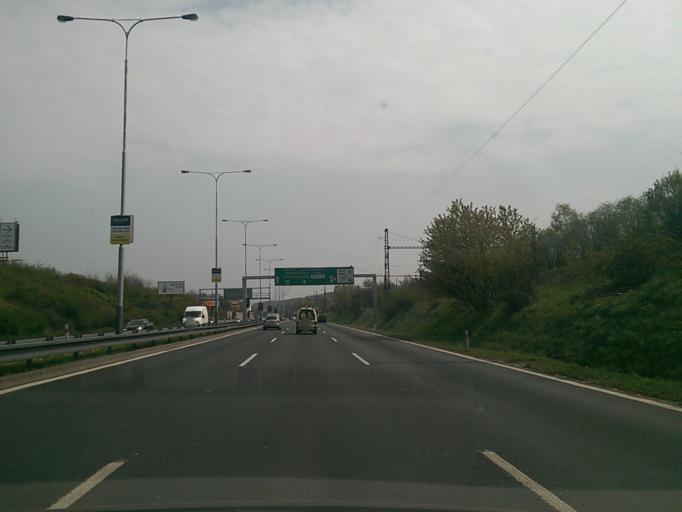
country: CZ
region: Praha
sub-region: Praha 4
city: Hodkovicky
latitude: 50.0328
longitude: 14.4315
